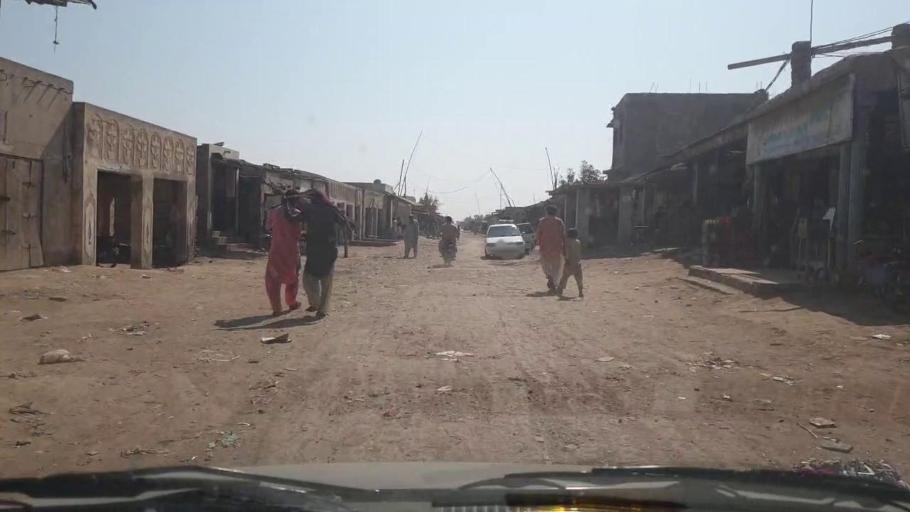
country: PK
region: Sindh
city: Samaro
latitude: 25.2776
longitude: 69.3410
